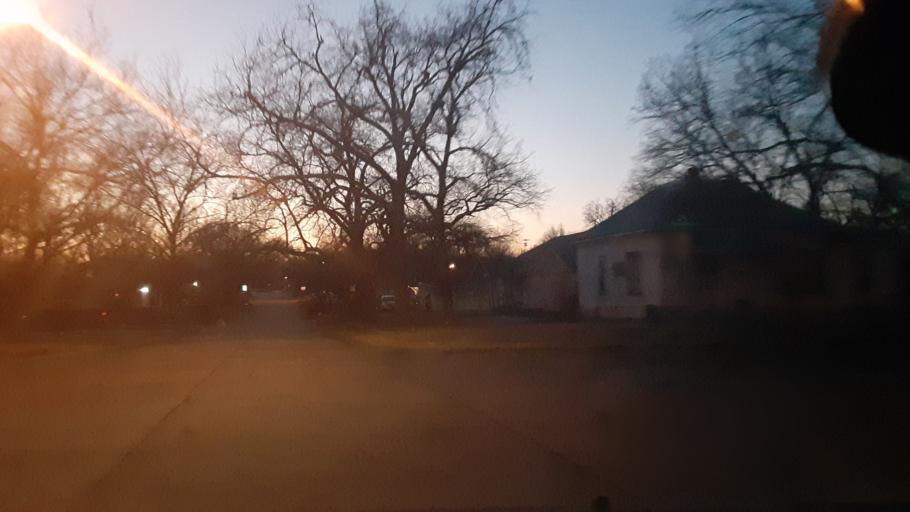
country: US
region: Oklahoma
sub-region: Payne County
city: Stillwater
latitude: 36.1113
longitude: -97.0708
